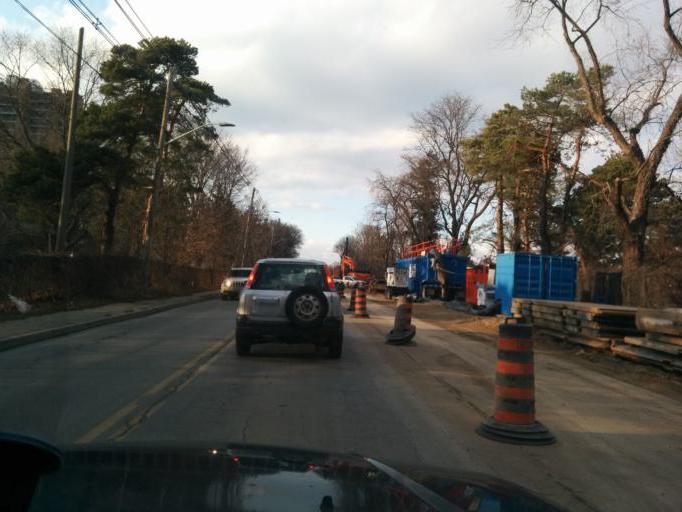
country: CA
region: Ontario
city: Etobicoke
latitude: 43.5895
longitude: -79.5583
